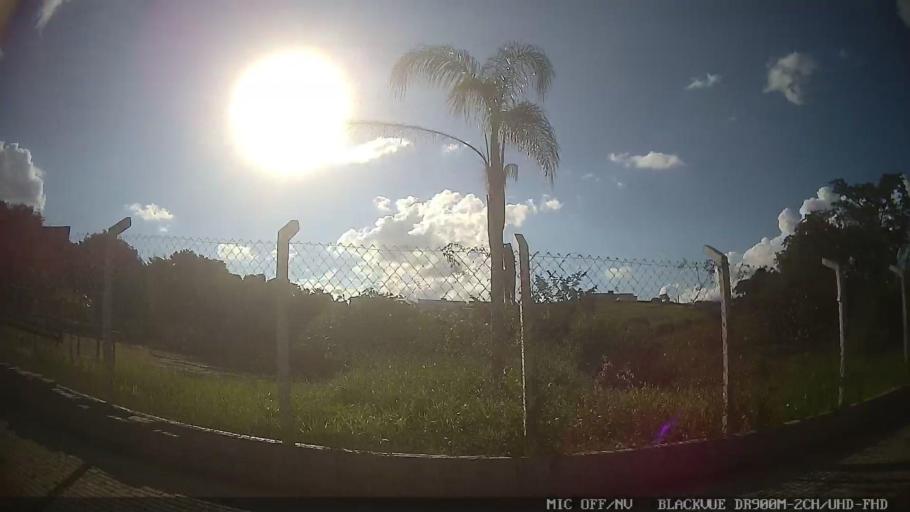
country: BR
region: Minas Gerais
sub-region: Extrema
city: Extrema
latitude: -22.8439
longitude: -46.3227
